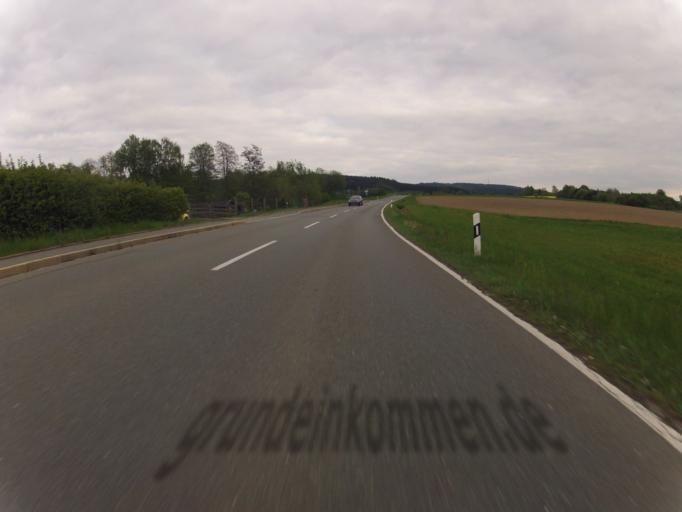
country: DE
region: Bavaria
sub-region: Upper Franconia
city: Sparneck
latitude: 50.1600
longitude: 11.8488
